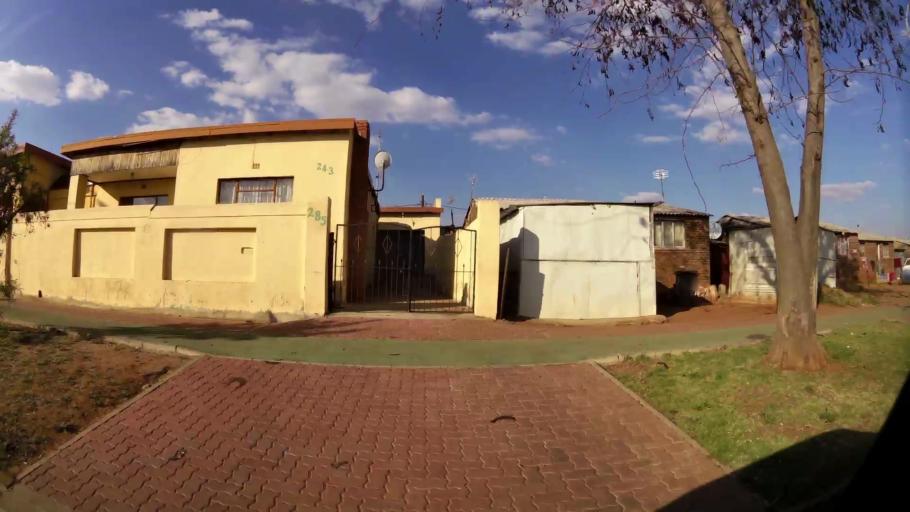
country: ZA
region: Gauteng
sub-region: City of Johannesburg Metropolitan Municipality
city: Roodepoort
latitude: -26.2076
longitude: 27.8842
